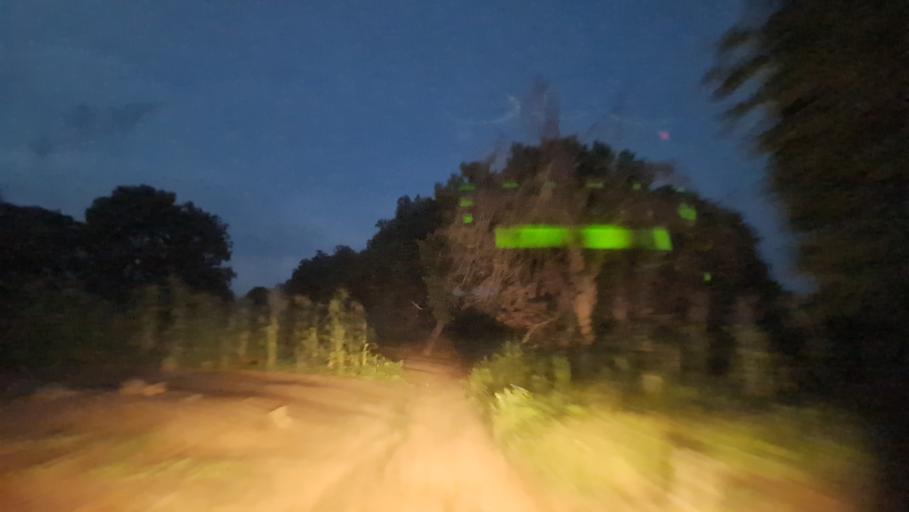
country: MZ
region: Nampula
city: Nampula
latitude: -14.6729
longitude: 39.8330
